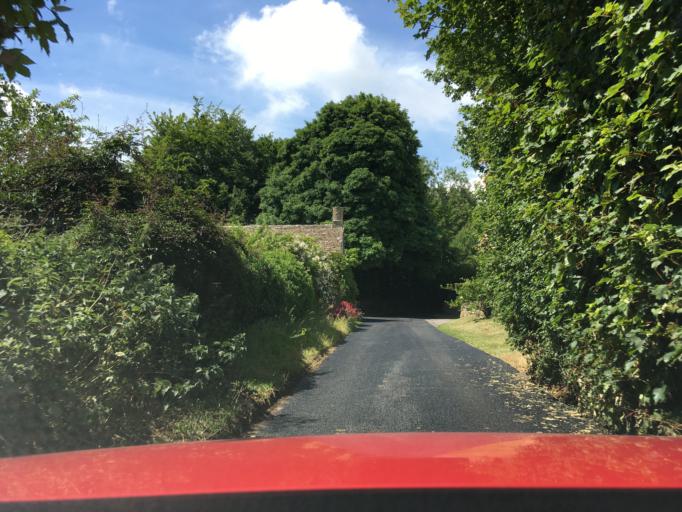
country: GB
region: England
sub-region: Gloucestershire
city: Tetbury
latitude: 51.6534
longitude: -2.1831
